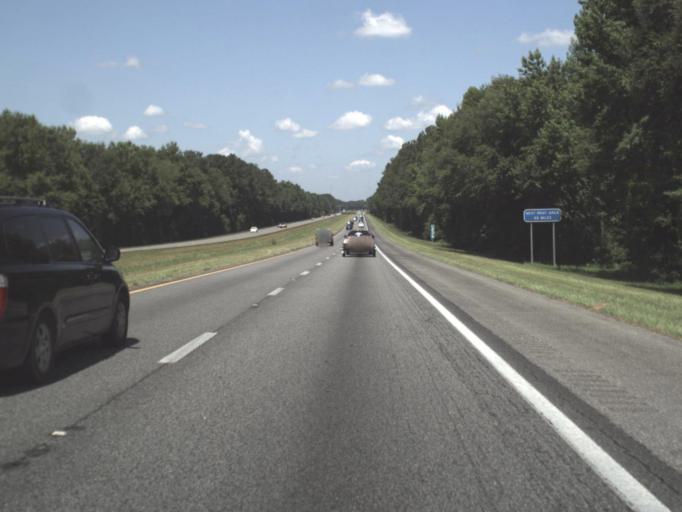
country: US
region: Florida
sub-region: Jefferson County
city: Monticello
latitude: 30.4453
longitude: -83.7117
